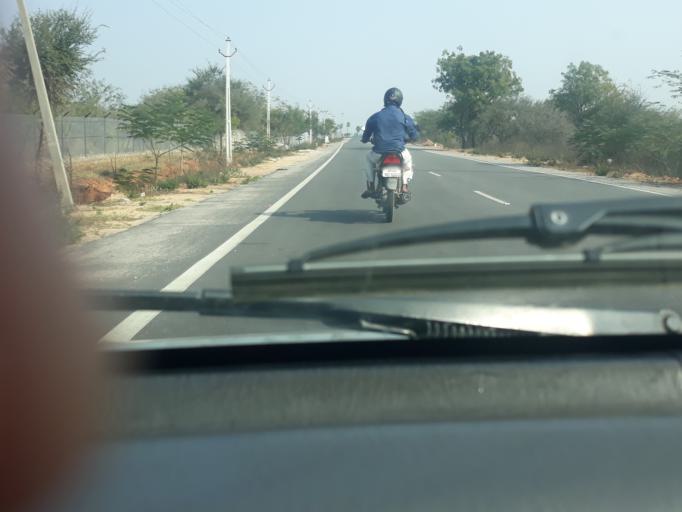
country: IN
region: Telangana
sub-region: Rangareddi
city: Lal Bahadur Nagar
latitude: 17.3583
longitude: 78.6203
